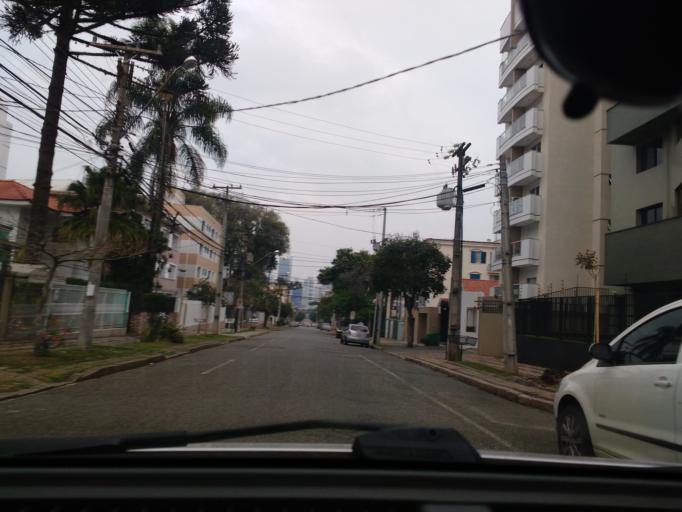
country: BR
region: Parana
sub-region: Curitiba
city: Curitiba
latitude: -25.4262
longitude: -49.2843
